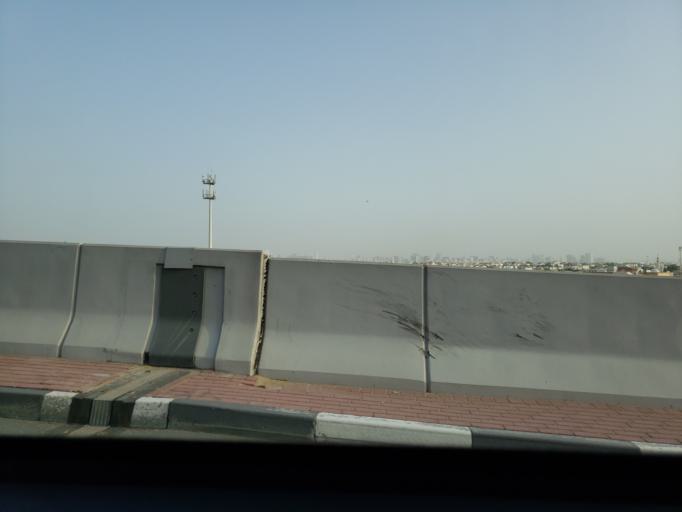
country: AE
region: Ash Shariqah
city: Sharjah
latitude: 25.3366
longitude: 55.4656
